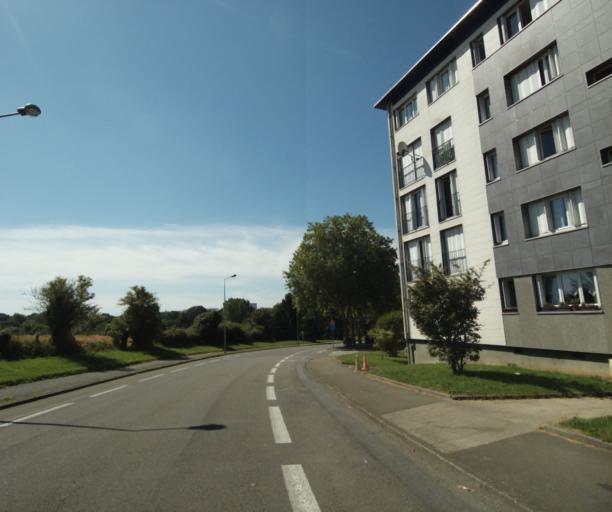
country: FR
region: Pays de la Loire
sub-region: Departement de la Mayenne
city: Laval
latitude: 48.0684
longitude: -0.7487
